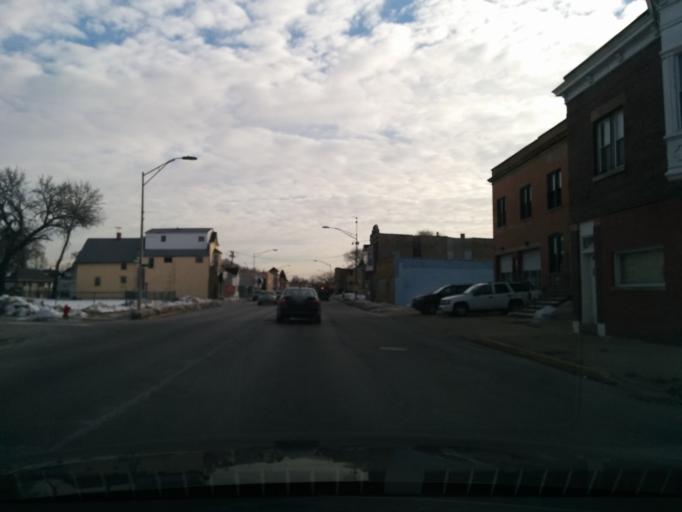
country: US
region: Illinois
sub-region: Cook County
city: Bellwood
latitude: 41.8876
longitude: -87.8676
